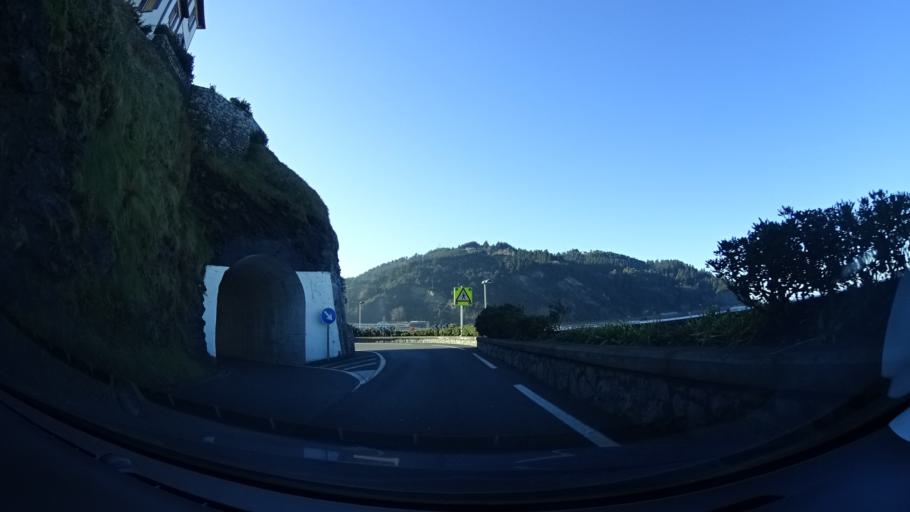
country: ES
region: Basque Country
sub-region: Provincia de Guipuzcoa
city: Deba
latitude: 43.2933
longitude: -2.3485
